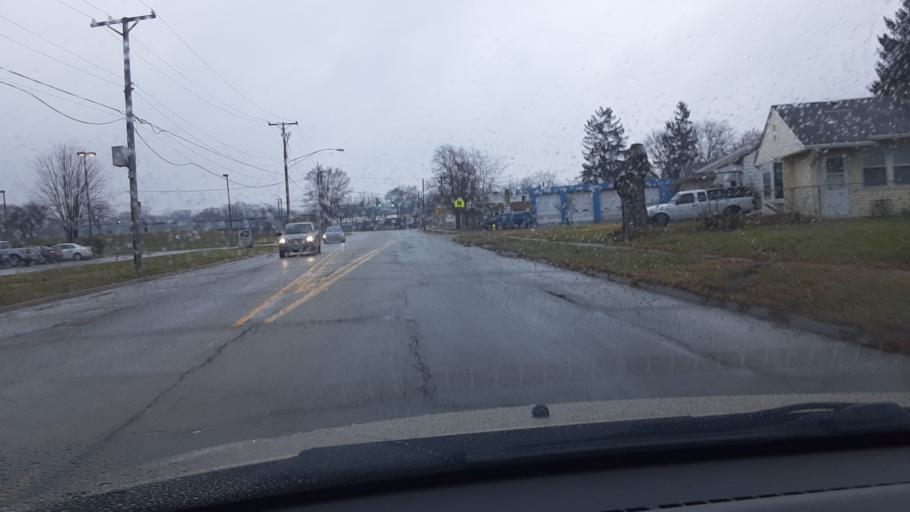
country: US
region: Illinois
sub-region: Winnebago County
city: Rockford
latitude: 42.2972
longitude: -89.1068
